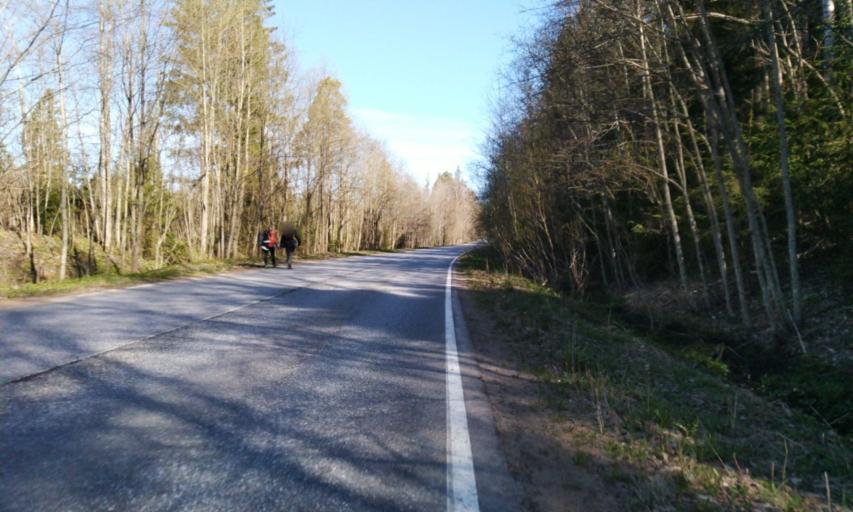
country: RU
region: Leningrad
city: Garbolovo
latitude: 60.3629
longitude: 30.4434
